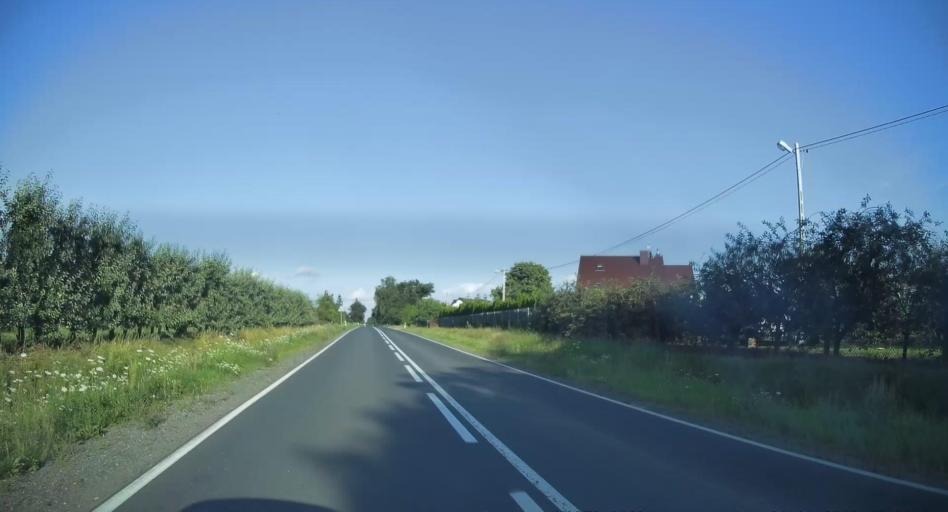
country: PL
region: Masovian Voivodeship
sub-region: Powiat grojecki
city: Bledow
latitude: 51.8034
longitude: 20.5975
